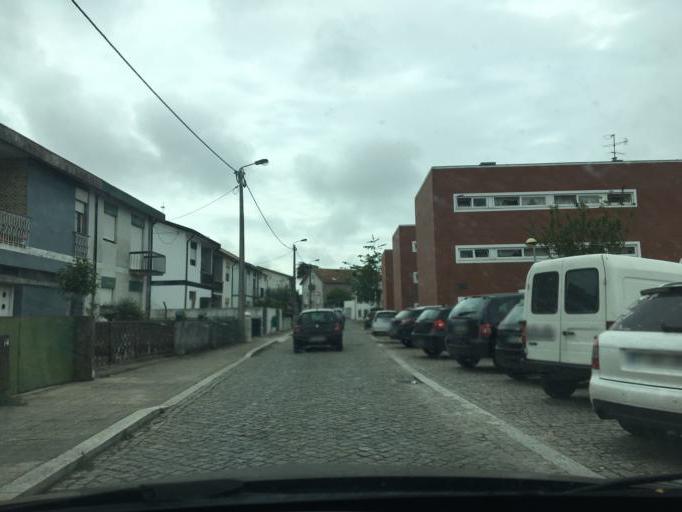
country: PT
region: Porto
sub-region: Matosinhos
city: Santa Cruz do Bispo
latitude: 41.2214
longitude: -8.6769
